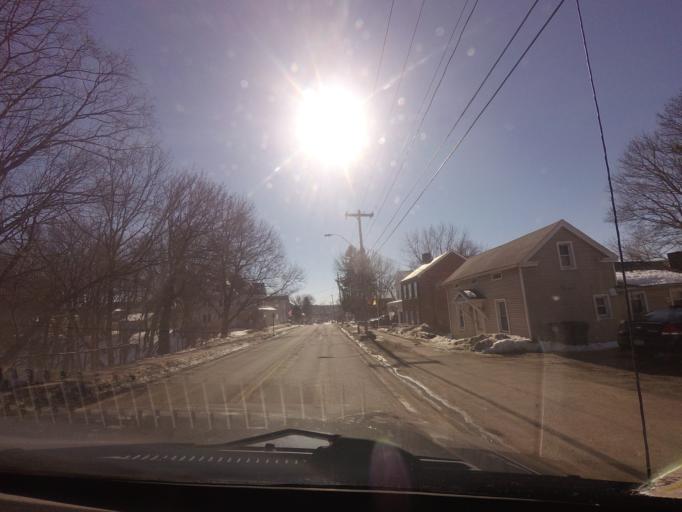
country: US
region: New York
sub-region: Saratoga County
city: Stillwater
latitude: 42.8990
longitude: -73.5859
